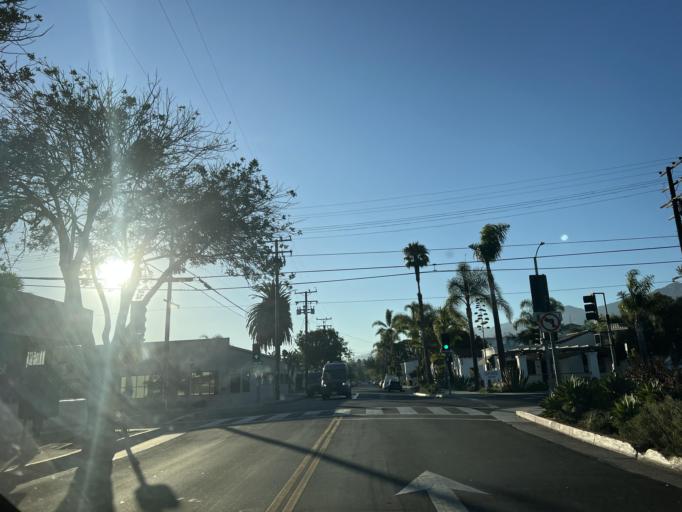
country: US
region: California
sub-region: Santa Barbara County
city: Santa Barbara
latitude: 34.4209
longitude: -119.6908
